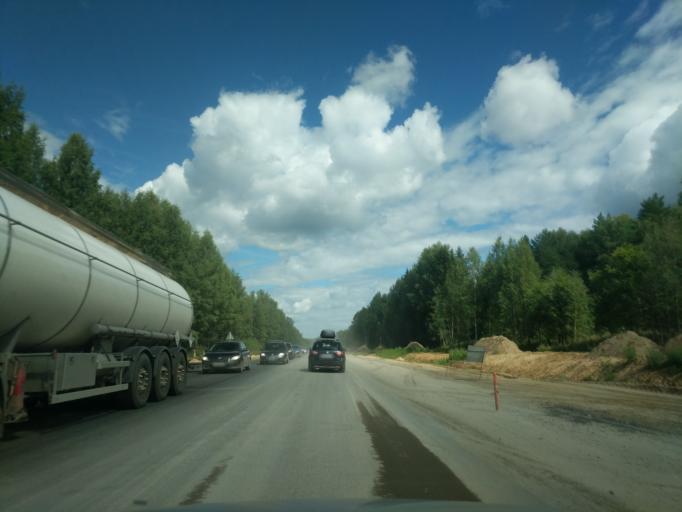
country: RU
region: Jaroslavl
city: Levashevo
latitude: 57.6595
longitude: 40.5672
